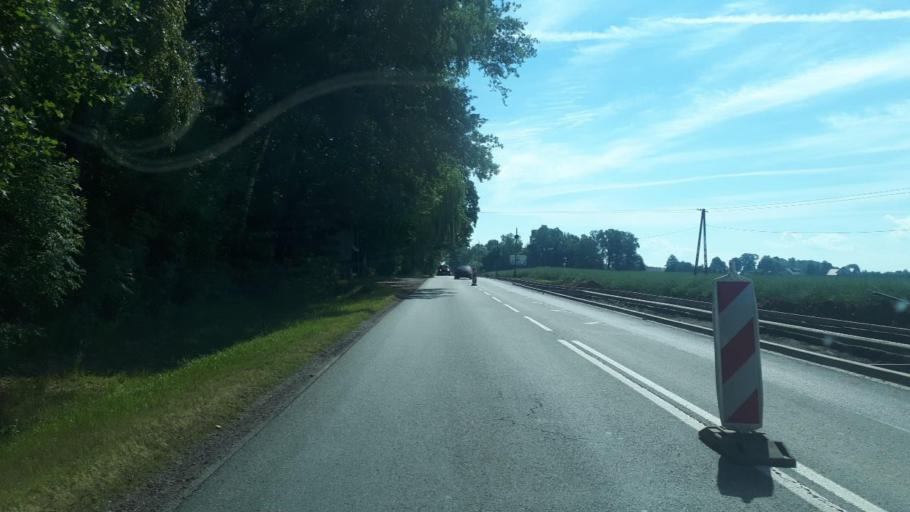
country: PL
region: Silesian Voivodeship
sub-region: Powiat pszczynski
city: Miedzna
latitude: 49.9705
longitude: 19.0206
